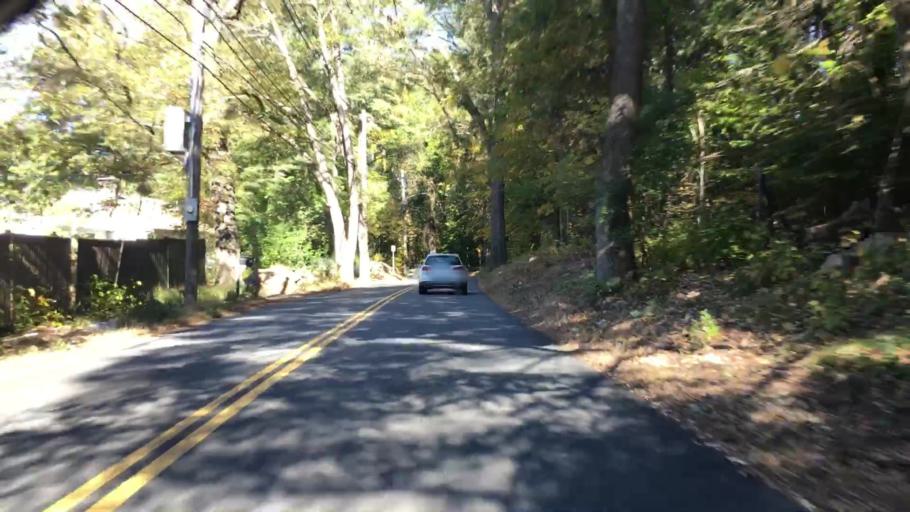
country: US
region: Massachusetts
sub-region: Middlesex County
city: Framingham Center
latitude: 42.2919
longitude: -71.4644
